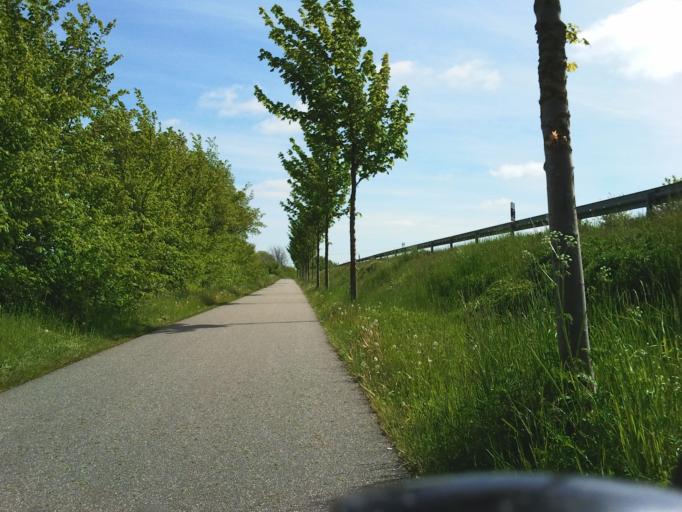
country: DE
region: Mecklenburg-Vorpommern
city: Papendorf
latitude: 54.0517
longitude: 12.1182
